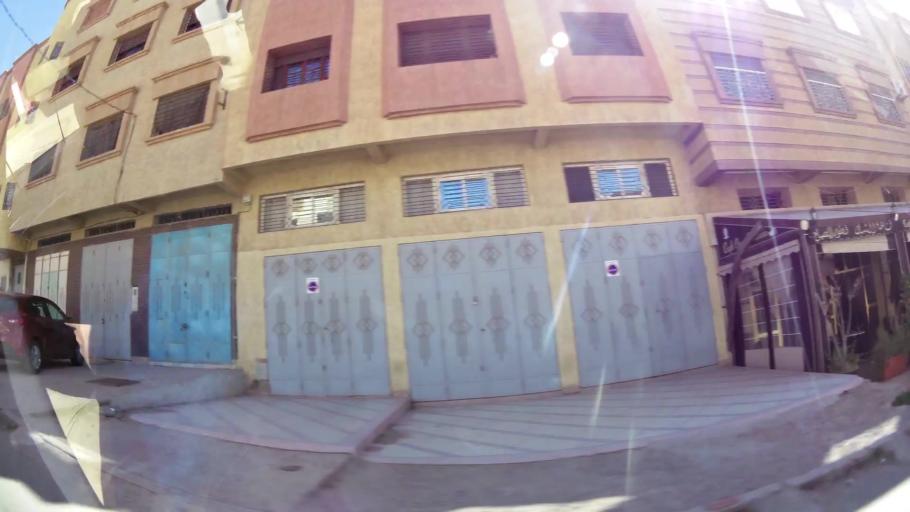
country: MA
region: Oriental
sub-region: Oujda-Angad
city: Oujda
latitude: 34.6585
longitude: -1.9192
